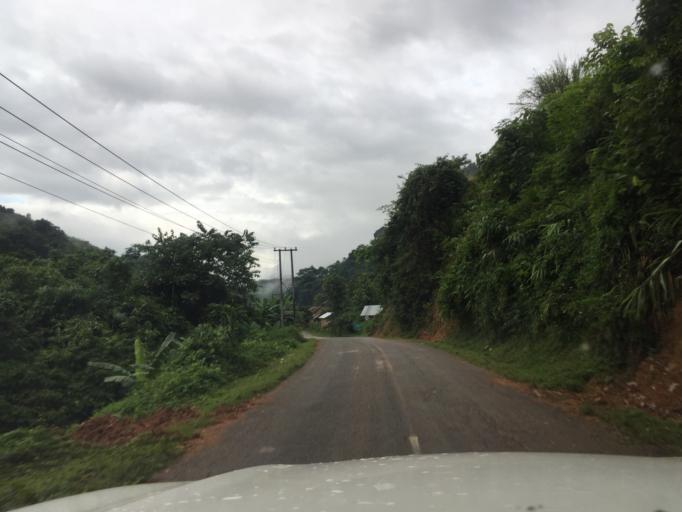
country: LA
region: Oudomxai
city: Muang La
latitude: 20.9121
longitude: 102.1888
